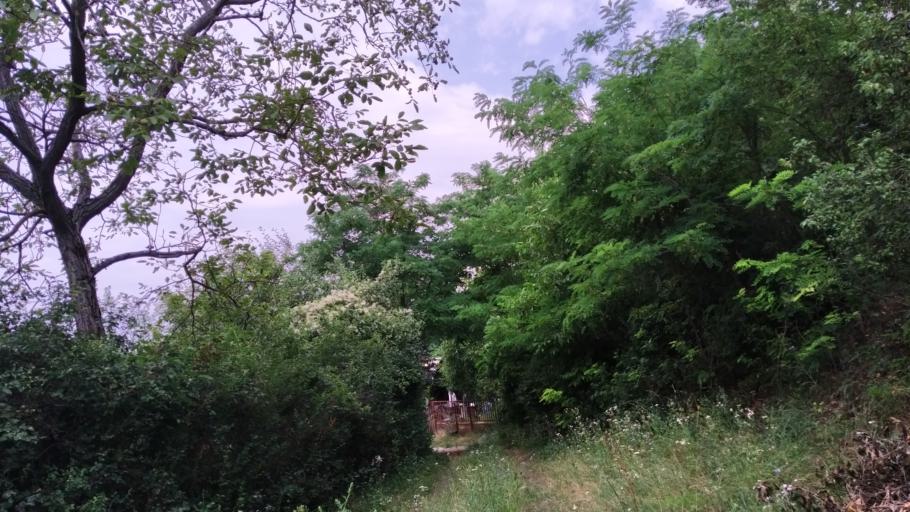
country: HU
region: Pest
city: Szob
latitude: 47.9332
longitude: 18.8270
